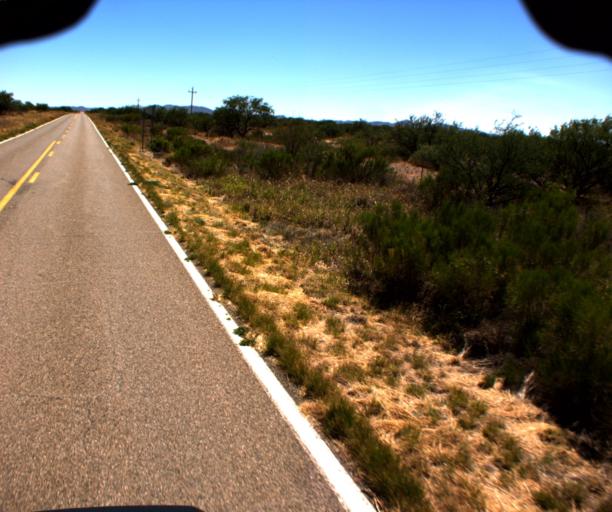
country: US
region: Arizona
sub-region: Pima County
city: Arivaca Junction
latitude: 31.6364
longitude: -111.5046
